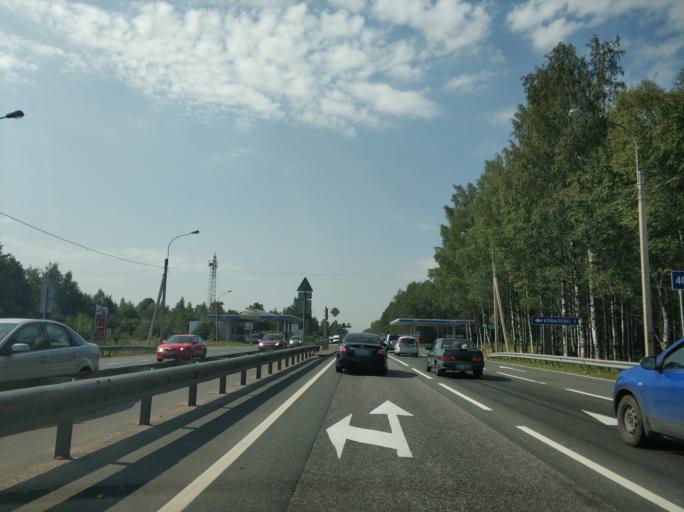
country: RU
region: St.-Petersburg
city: Krasnogvargeisky
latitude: 59.9948
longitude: 30.5401
